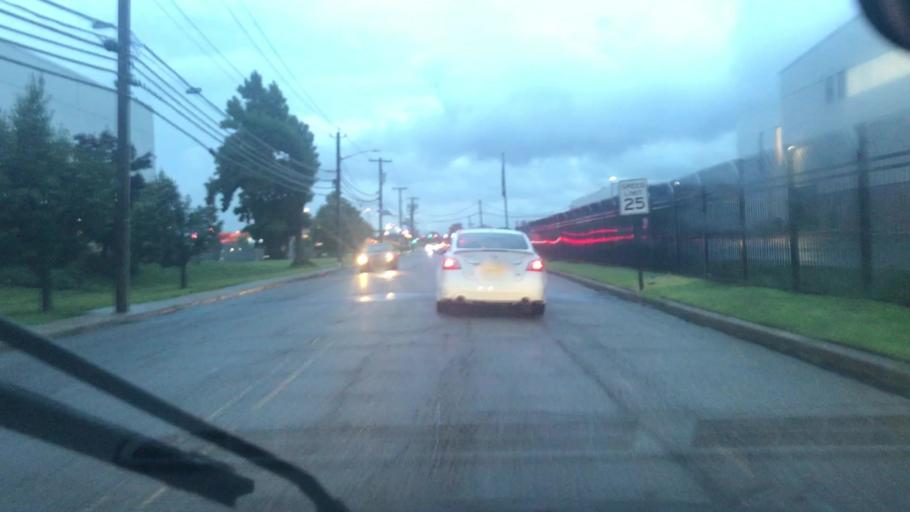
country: US
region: New Jersey
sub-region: Bergen County
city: Hasbrouck Heights
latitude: 40.8579
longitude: -74.0625
